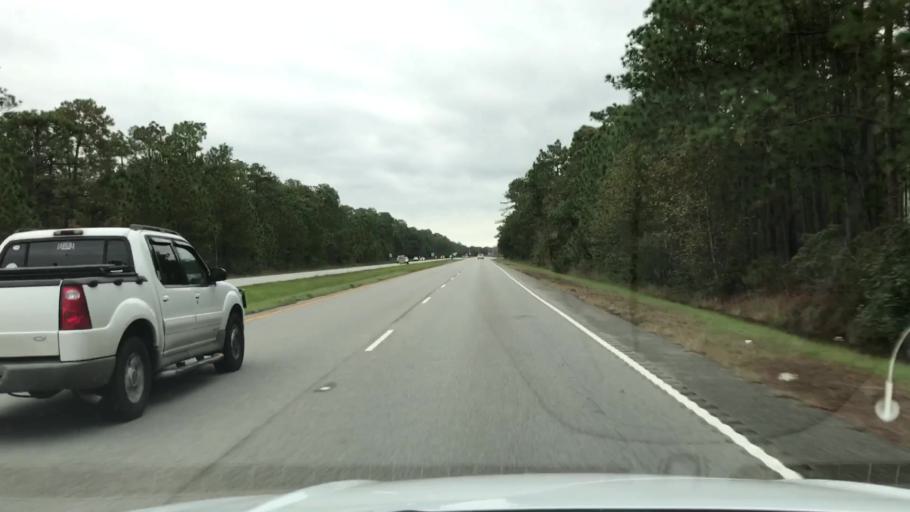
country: US
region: South Carolina
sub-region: Georgetown County
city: Georgetown
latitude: 33.4101
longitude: -79.1914
